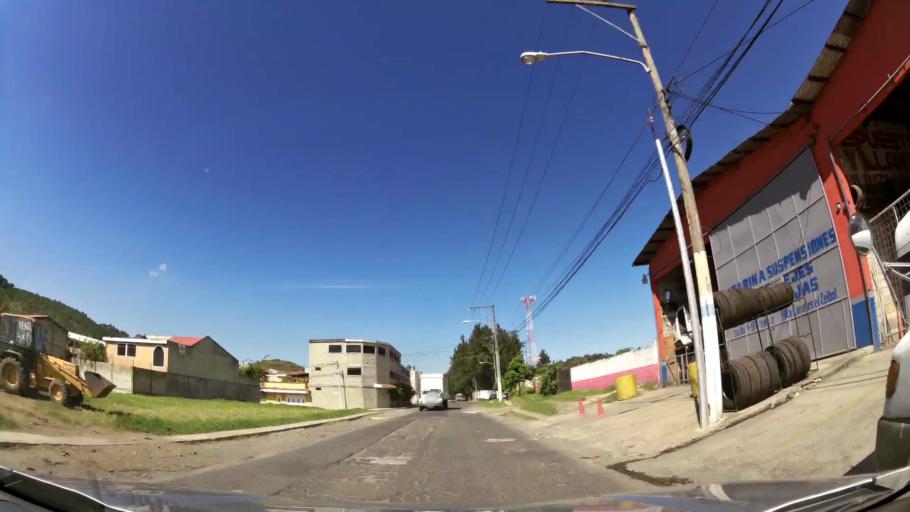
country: GT
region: Guatemala
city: Villa Canales
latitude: 14.4775
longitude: -90.5335
